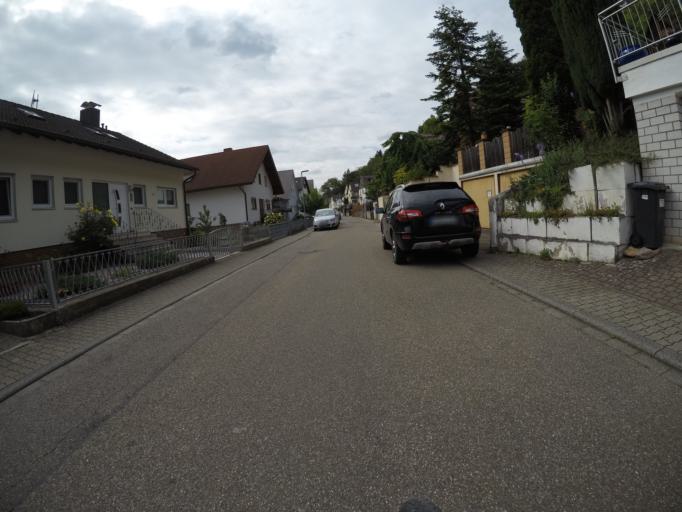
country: DE
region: Baden-Wuerttemberg
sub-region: Karlsruhe Region
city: Joehlingen
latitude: 48.9825
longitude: 8.5526
